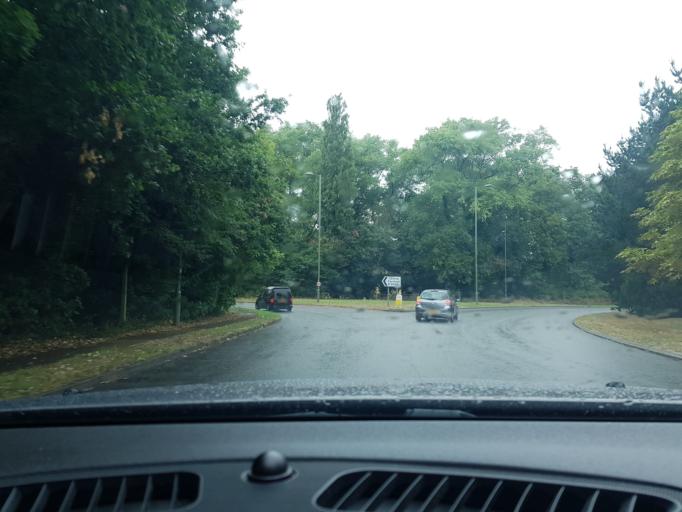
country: GB
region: England
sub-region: Surrey
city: Hale
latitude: 51.2249
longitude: -0.7828
